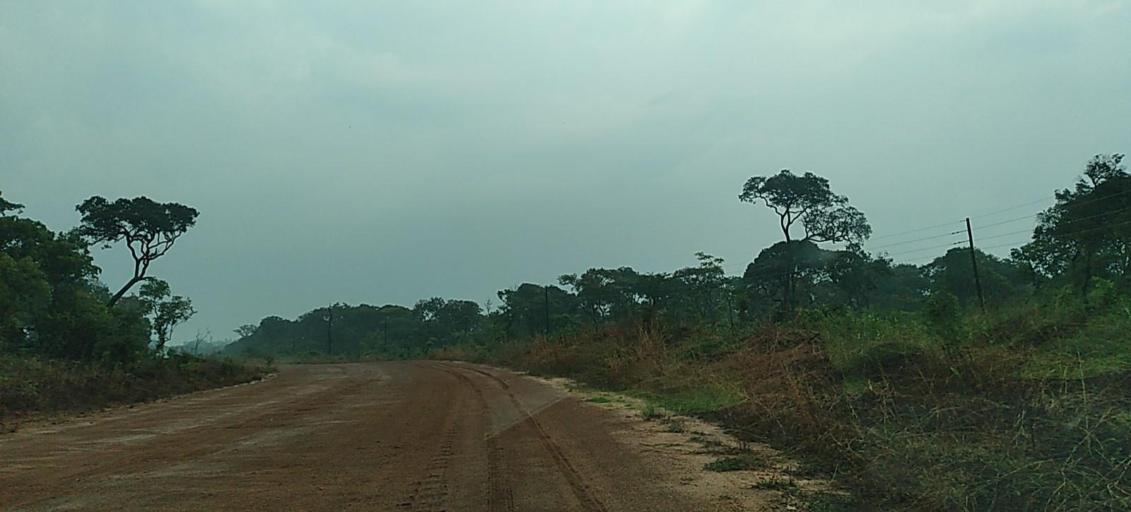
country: ZM
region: North-Western
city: Mwinilunga
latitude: -11.5887
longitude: 24.3869
